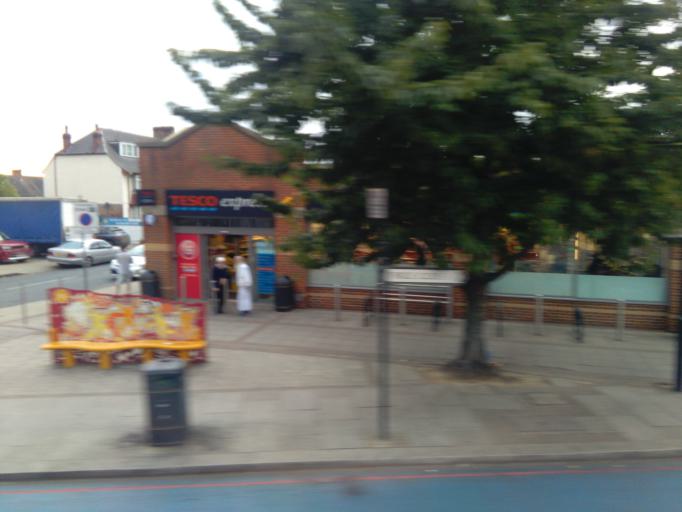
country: GB
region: England
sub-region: Greater London
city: Earlsfield
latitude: 51.4328
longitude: -0.1638
